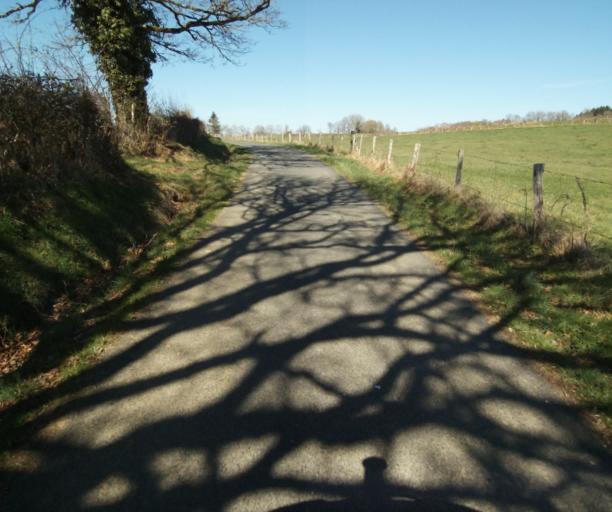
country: FR
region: Limousin
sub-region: Departement de la Correze
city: Chamboulive
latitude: 45.4567
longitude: 1.6881
